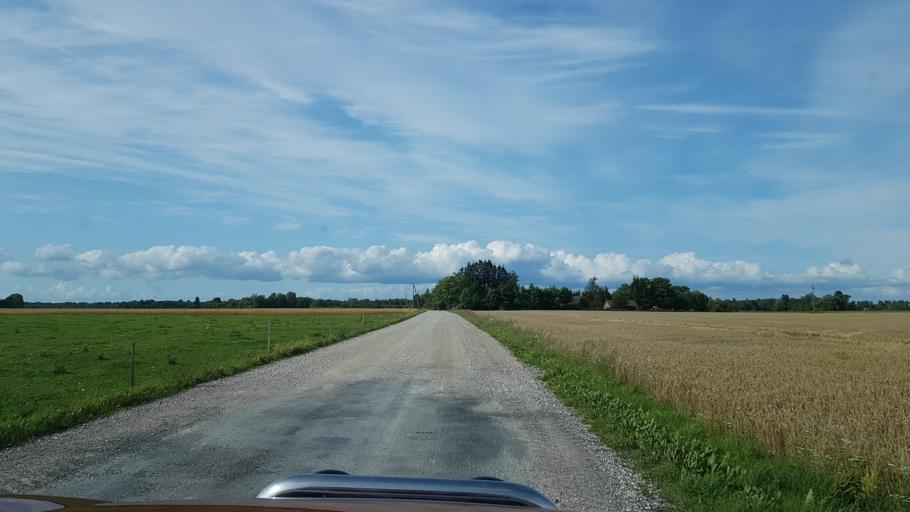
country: EE
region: Laeaene
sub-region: Lihula vald
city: Lihula
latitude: 58.4517
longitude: 23.9961
